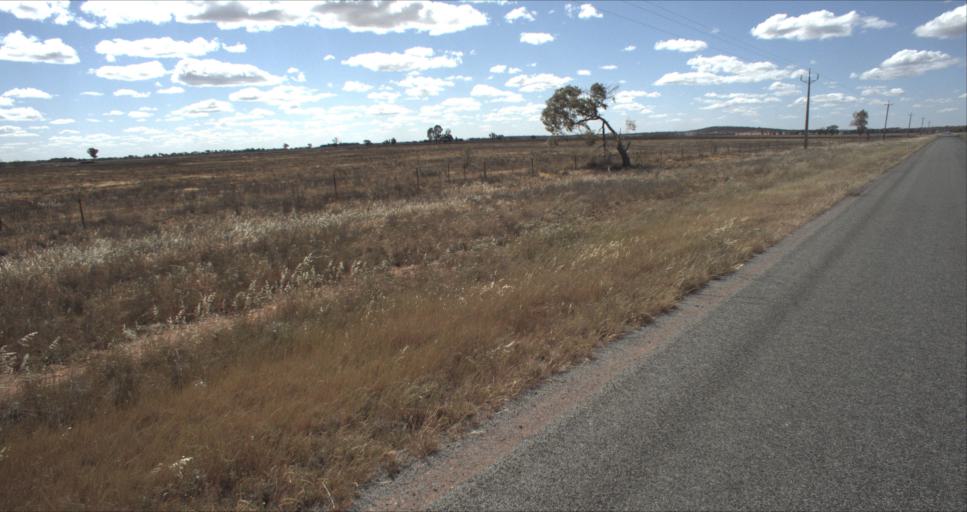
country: AU
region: New South Wales
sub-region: Leeton
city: Leeton
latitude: -34.4568
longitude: 146.2535
